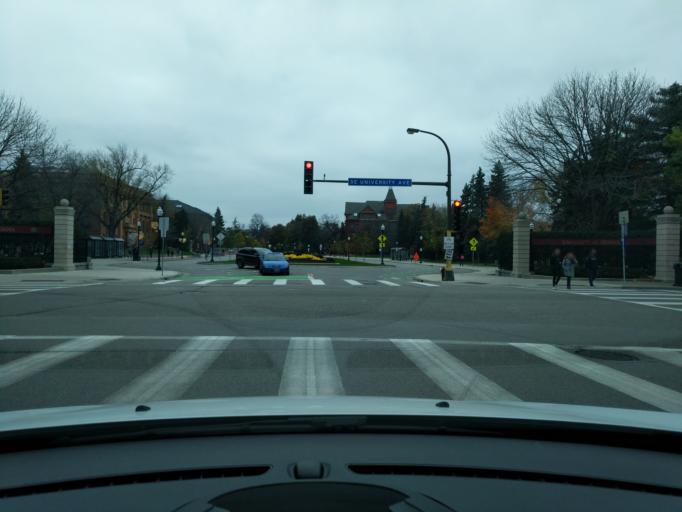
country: US
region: Minnesota
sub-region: Hennepin County
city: Minneapolis
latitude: 44.9791
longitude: -93.2351
